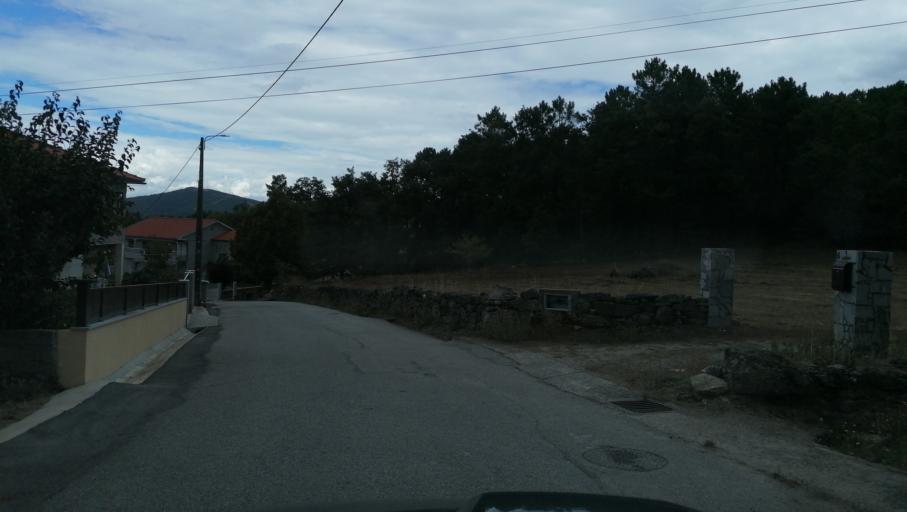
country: PT
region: Vila Real
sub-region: Vila Pouca de Aguiar
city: Vila Pouca de Aguiar
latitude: 41.5592
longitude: -7.6469
